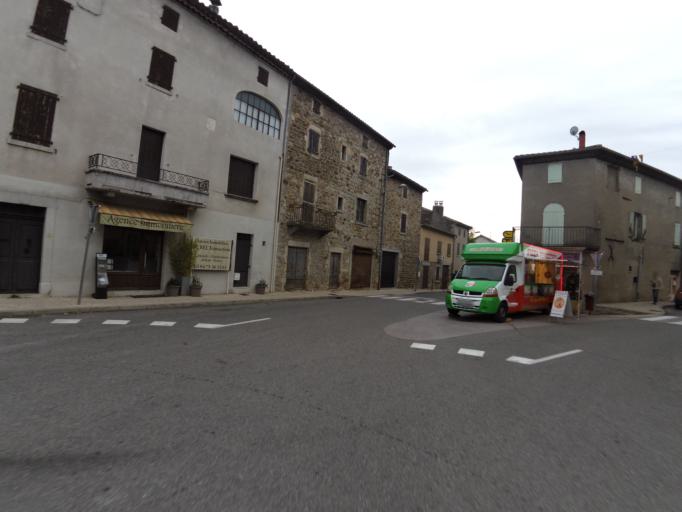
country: FR
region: Rhone-Alpes
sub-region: Departement de l'Ardeche
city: Lablachere
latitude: 44.4639
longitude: 4.2148
